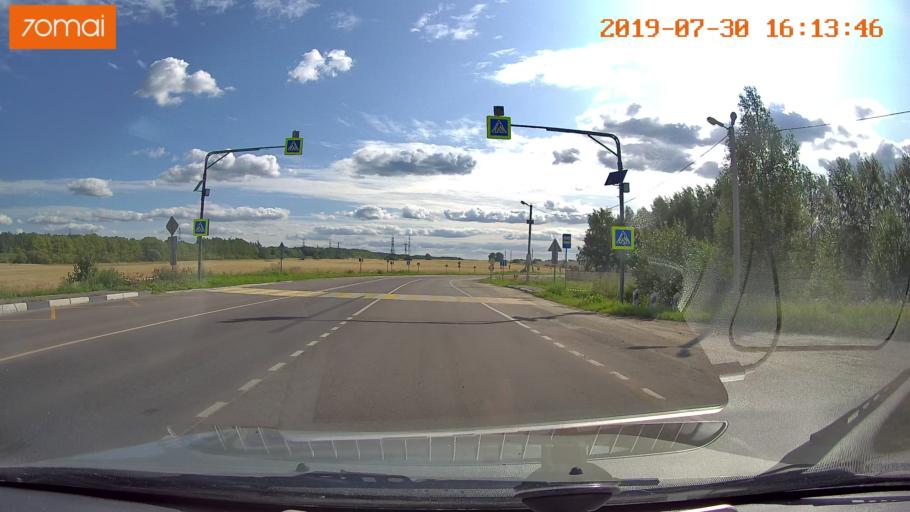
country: RU
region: Moskovskaya
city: Voskresensk
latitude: 55.2887
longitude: 38.6894
